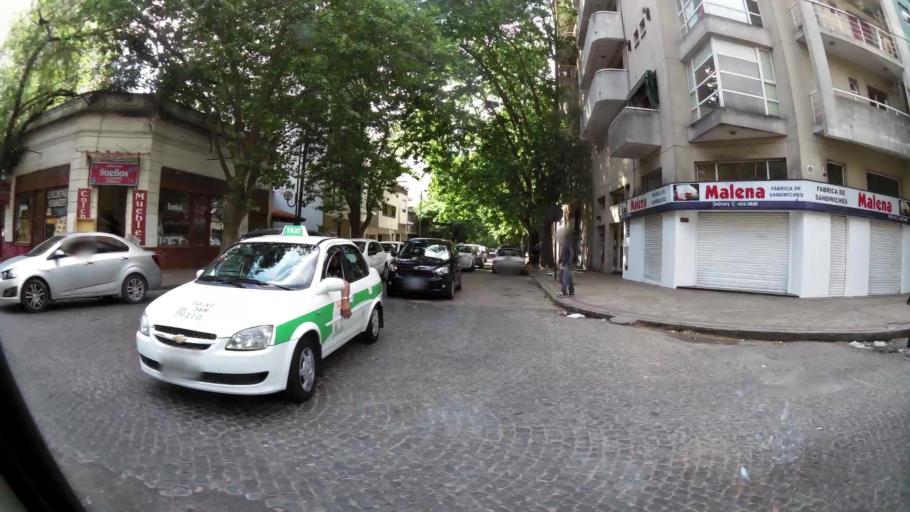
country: AR
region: Buenos Aires
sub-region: Partido de La Plata
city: La Plata
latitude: -34.9162
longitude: -57.9364
